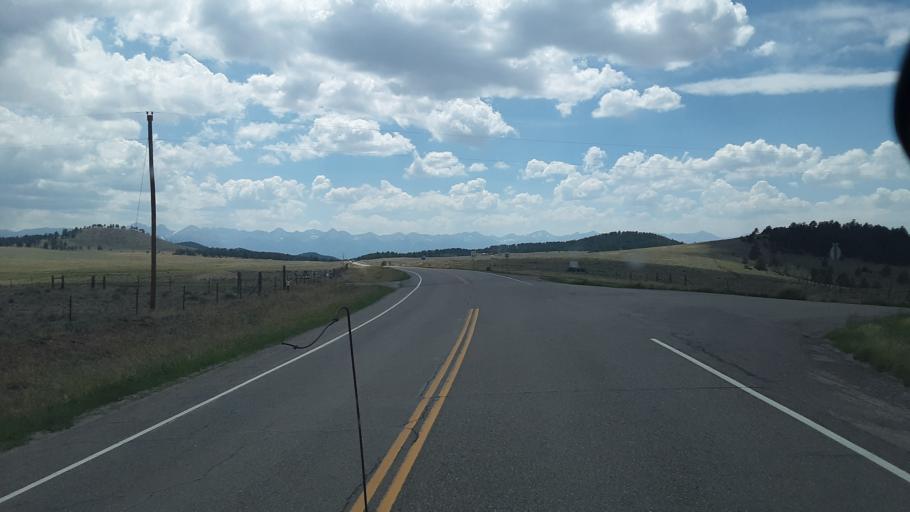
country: US
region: Colorado
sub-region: Custer County
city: Westcliffe
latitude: 38.1635
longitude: -105.2888
